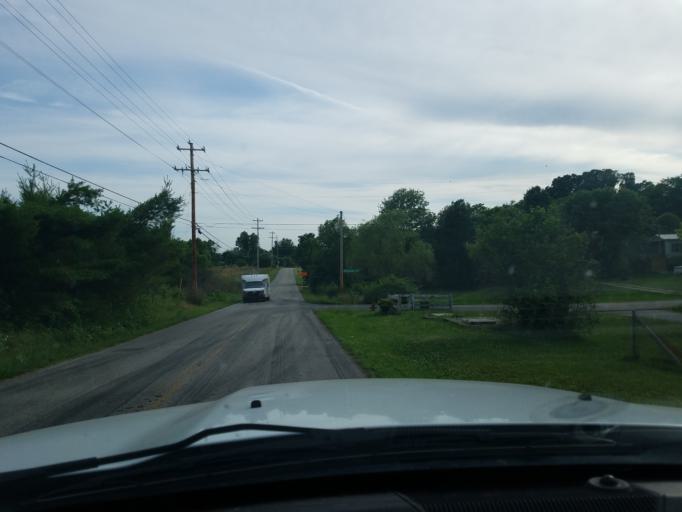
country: US
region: Tennessee
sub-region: Putnam County
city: Baxter
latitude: 36.1310
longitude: -85.5988
